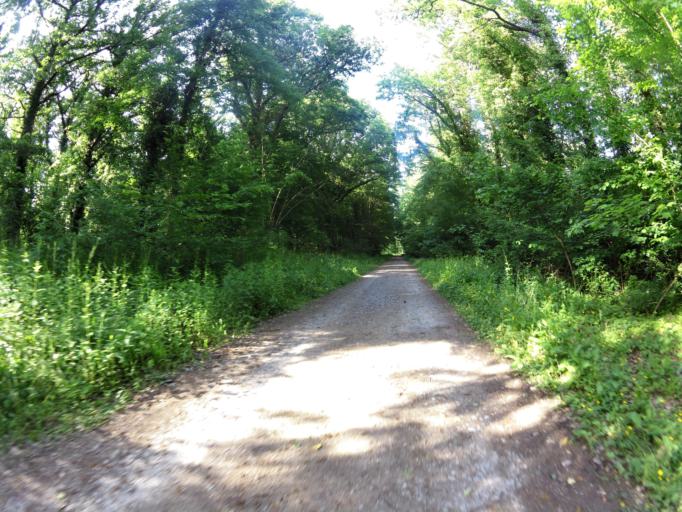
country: DE
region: Bavaria
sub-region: Regierungsbezirk Unterfranken
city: Ochsenfurt
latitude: 49.6827
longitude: 10.0694
